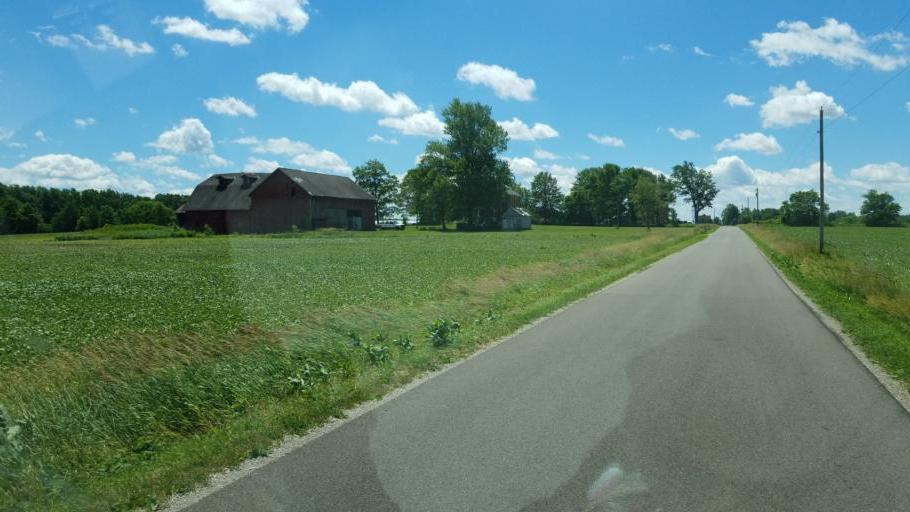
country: US
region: Ohio
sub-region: Crawford County
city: Galion
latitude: 40.7320
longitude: -82.8653
